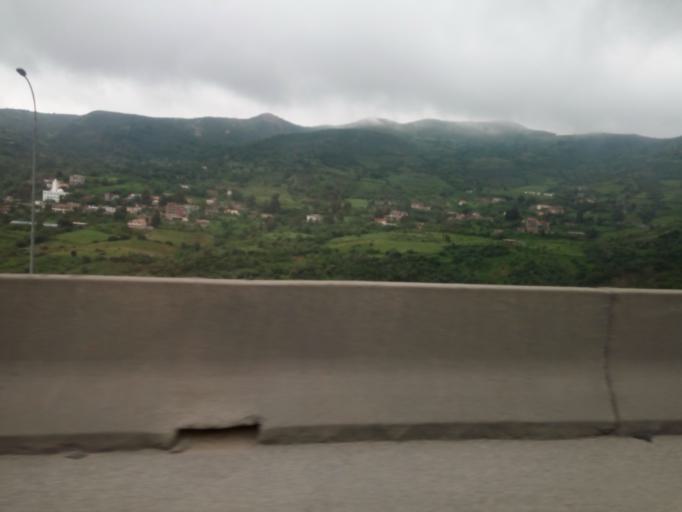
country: DZ
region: Bouira
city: Lakhdaria
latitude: 36.5905
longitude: 3.4909
